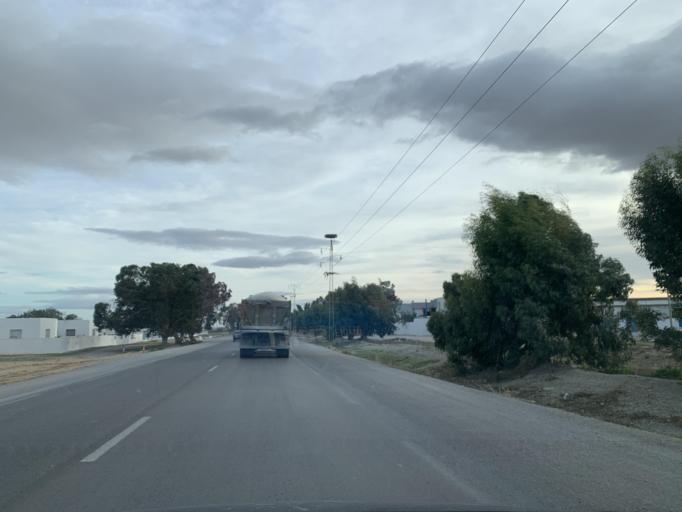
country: TN
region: Susah
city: Harqalah
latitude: 36.1072
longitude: 10.3870
